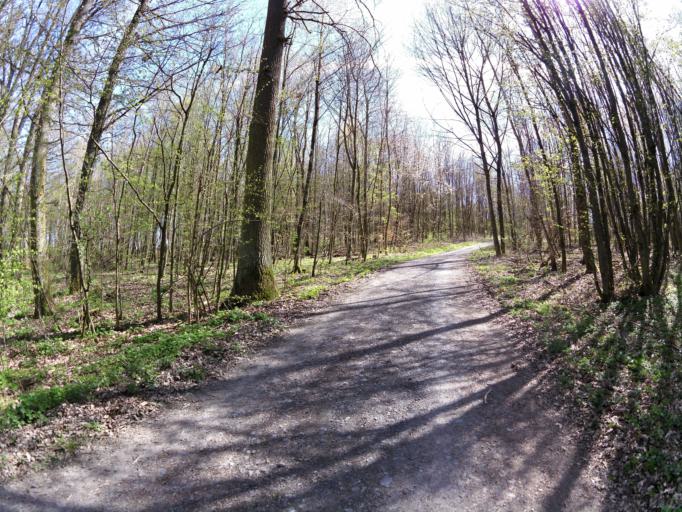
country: DE
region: Bavaria
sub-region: Regierungsbezirk Unterfranken
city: Hettstadt
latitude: 49.8124
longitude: 9.8024
